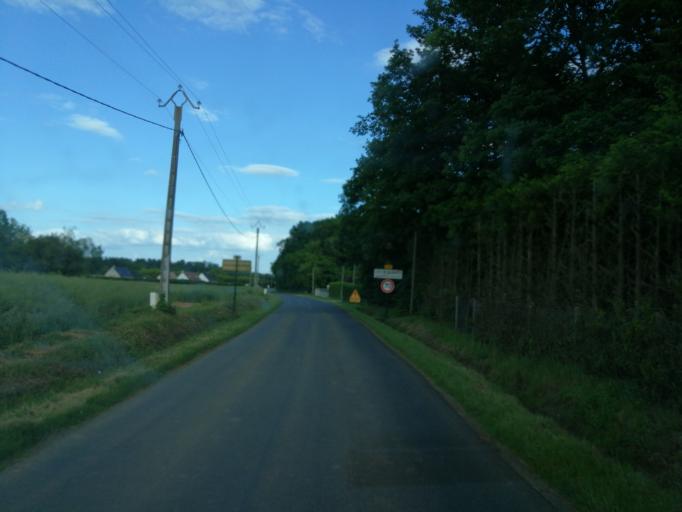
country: FR
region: Haute-Normandie
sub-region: Departement de l'Eure
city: Damville
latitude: 48.8534
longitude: 1.0868
